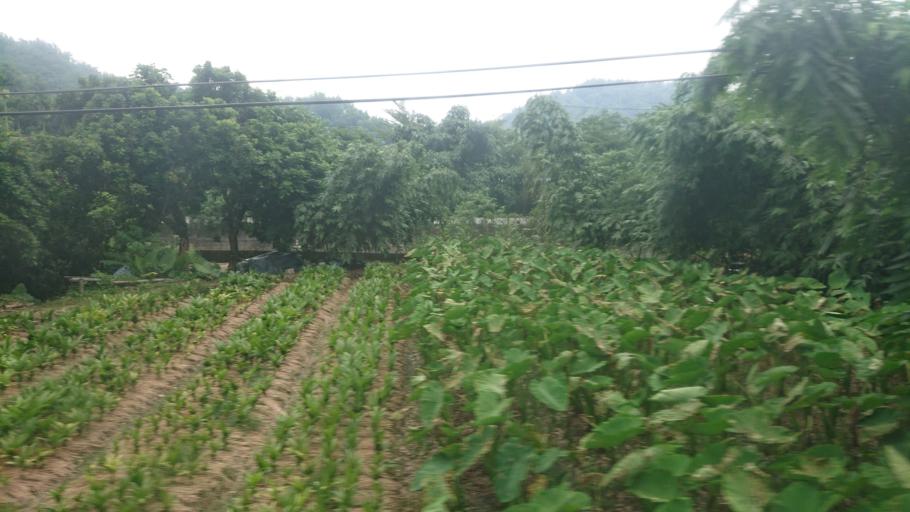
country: TW
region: Taiwan
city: Lugu
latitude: 23.8270
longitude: 120.7751
